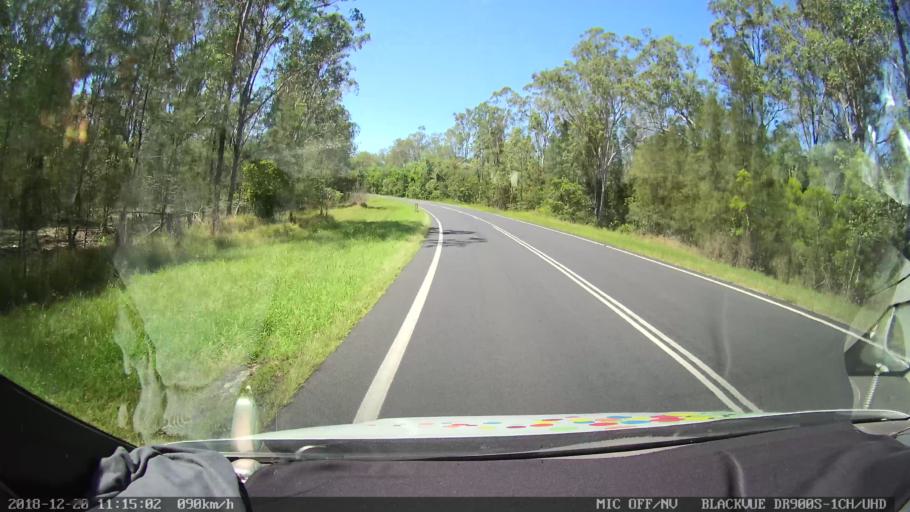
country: AU
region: New South Wales
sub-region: Richmond Valley
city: Casino
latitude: -29.0081
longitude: 153.0065
